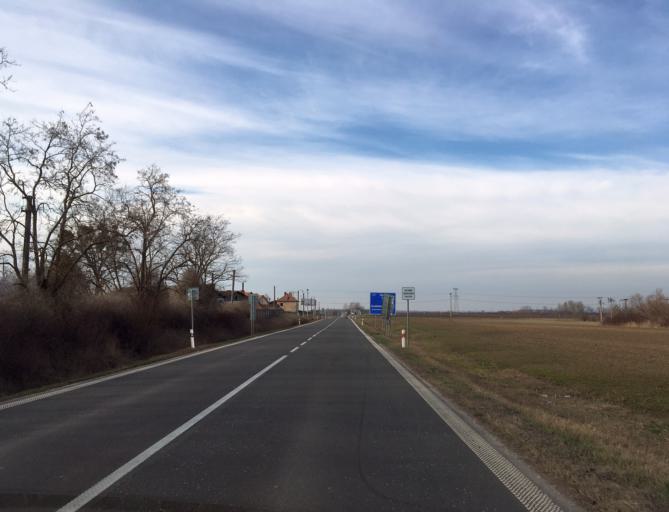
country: SK
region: Nitriansky
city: Surany
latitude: 48.0600
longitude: 18.1016
